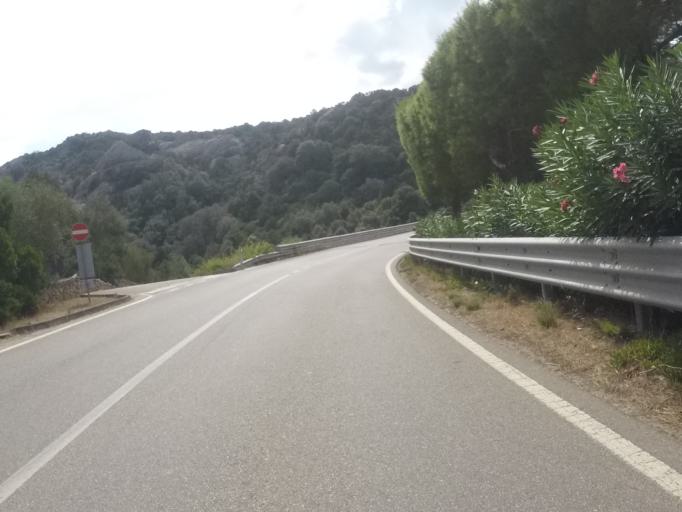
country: IT
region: Sardinia
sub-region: Provincia di Olbia-Tempio
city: Porto Cervo
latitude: 41.1344
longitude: 9.4976
